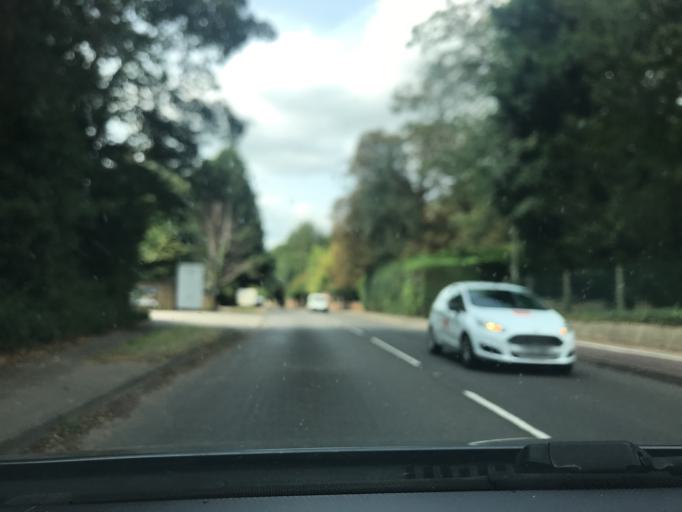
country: GB
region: England
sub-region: Surrey
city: Addlestone
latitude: 51.3773
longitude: -0.4830
